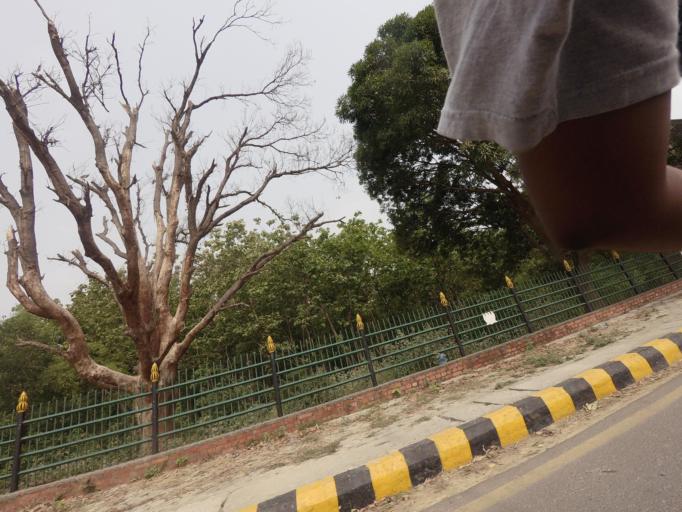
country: IN
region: Uttar Pradesh
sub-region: Maharajganj
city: Nautanwa
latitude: 27.4640
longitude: 83.2836
